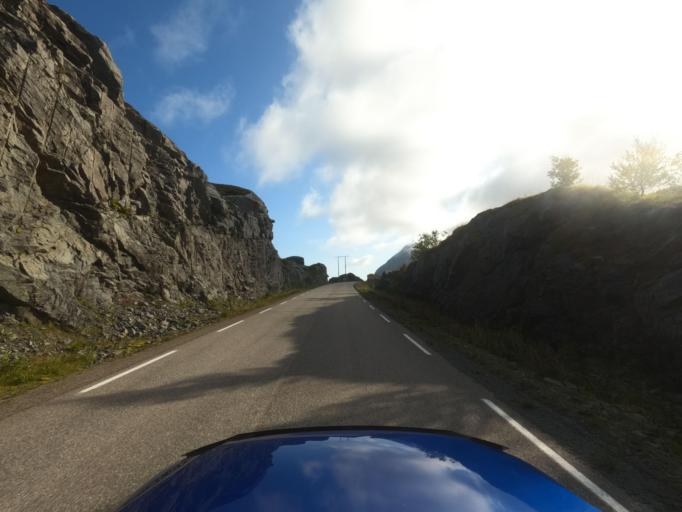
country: NO
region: Nordland
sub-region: Flakstad
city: Ramberg
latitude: 68.0220
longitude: 13.1849
